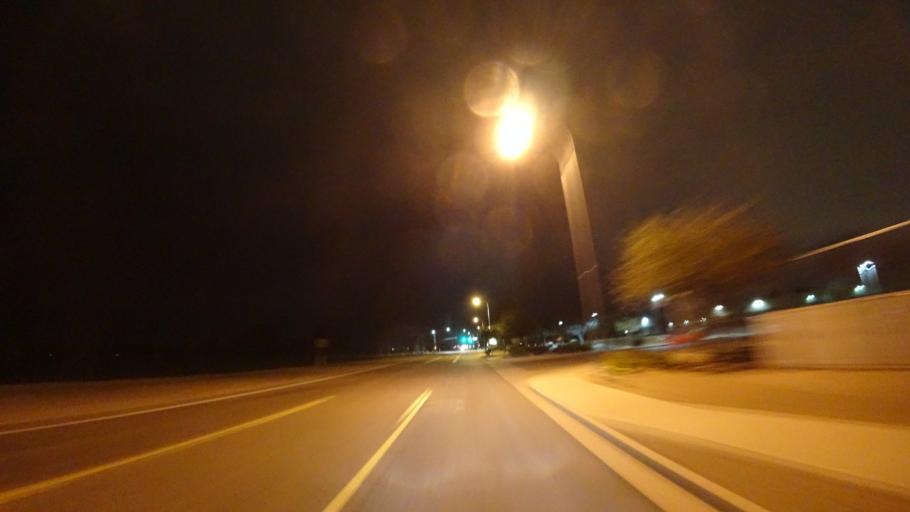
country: US
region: Arizona
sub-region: Maricopa County
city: Sun Lakes
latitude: 33.2336
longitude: -111.8133
